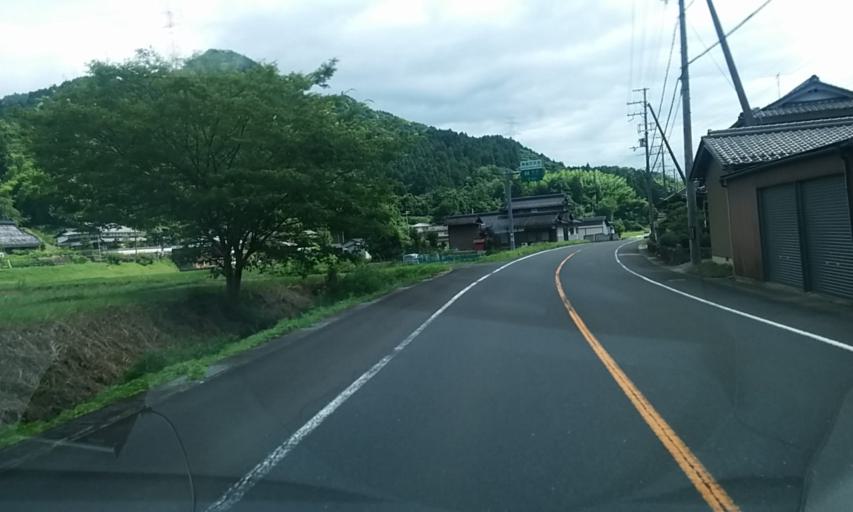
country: JP
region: Kyoto
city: Ayabe
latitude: 35.3408
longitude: 135.2715
